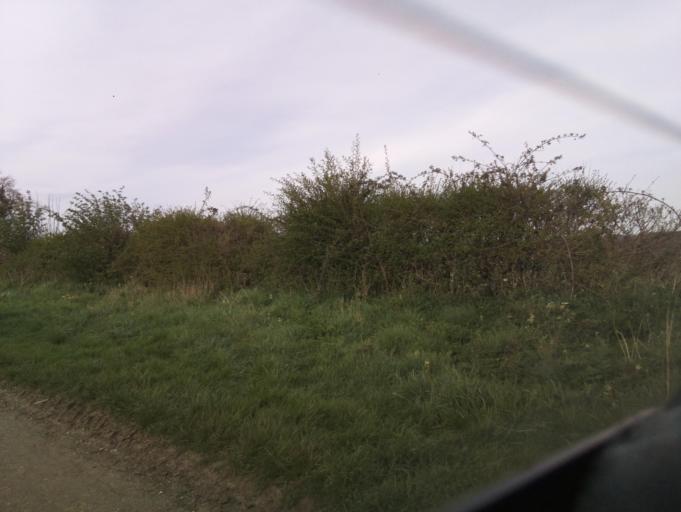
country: GB
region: England
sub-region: Somerset
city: Milborne Port
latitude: 50.9590
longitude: -2.4664
